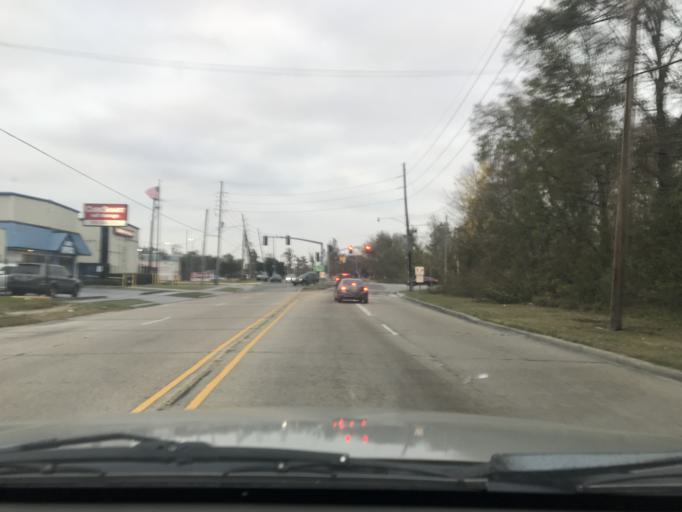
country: US
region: Louisiana
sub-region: Jefferson Parish
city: Woodmere
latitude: 29.8677
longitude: -90.0750
